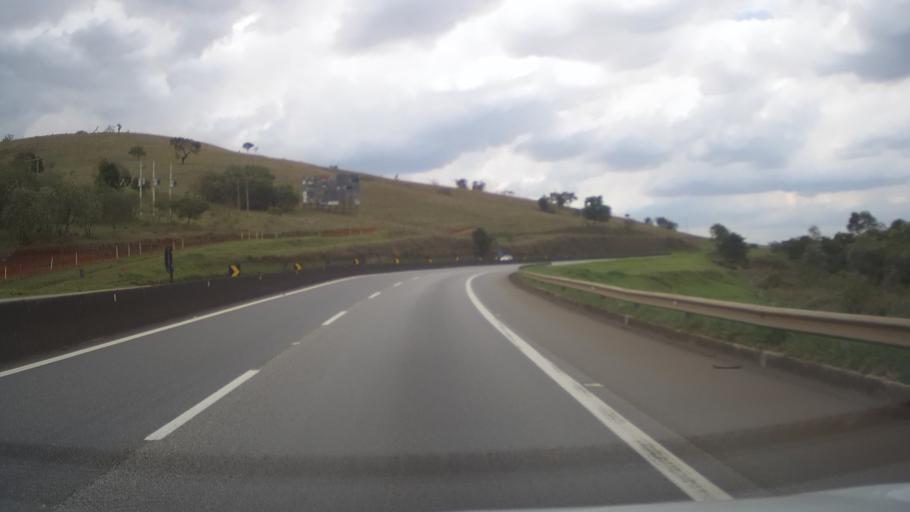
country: BR
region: Minas Gerais
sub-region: Tres Coracoes
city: Tres Coracoes
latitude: -21.5198
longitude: -45.2232
